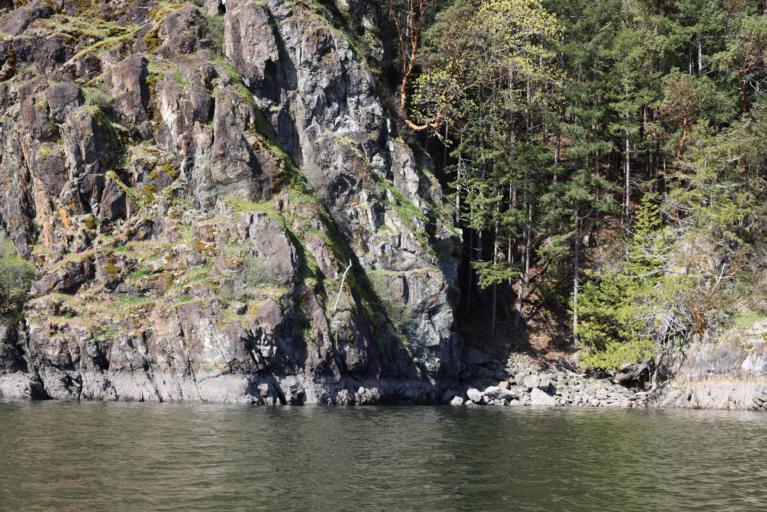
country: CA
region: British Columbia
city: Langford
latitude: 48.5631
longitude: -123.5195
